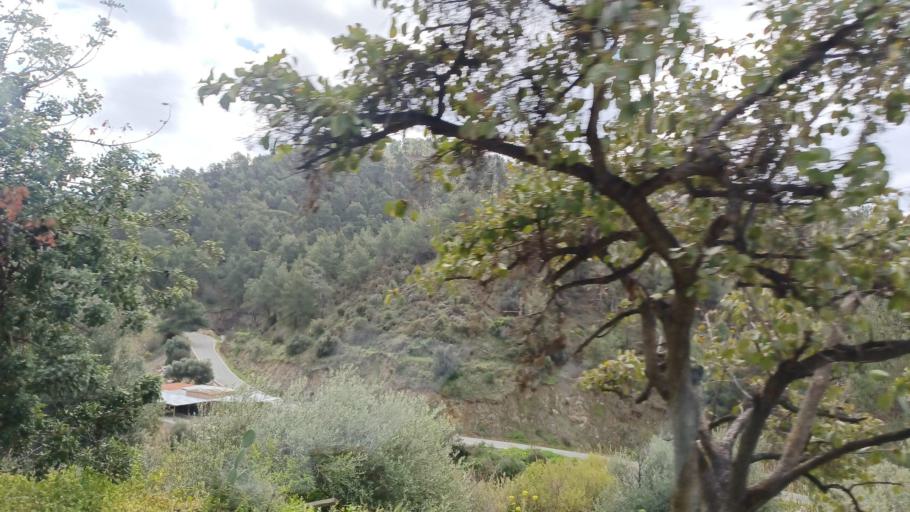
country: CY
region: Pafos
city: Polis
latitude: 35.1013
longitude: 32.5160
